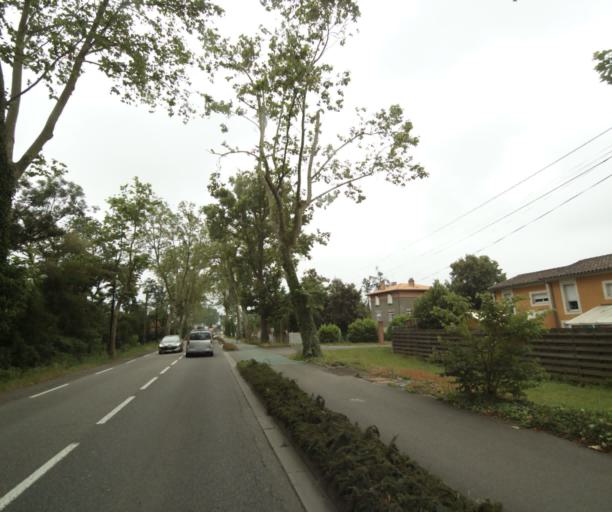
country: FR
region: Midi-Pyrenees
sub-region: Departement du Tarn-et-Garonne
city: Montauban
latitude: 43.9984
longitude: 1.3391
